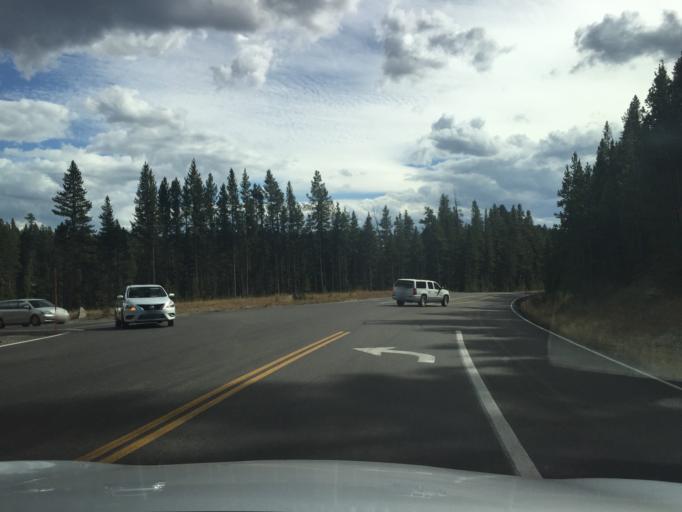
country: US
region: Montana
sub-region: Gallatin County
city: West Yellowstone
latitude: 44.7084
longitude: -110.5040
